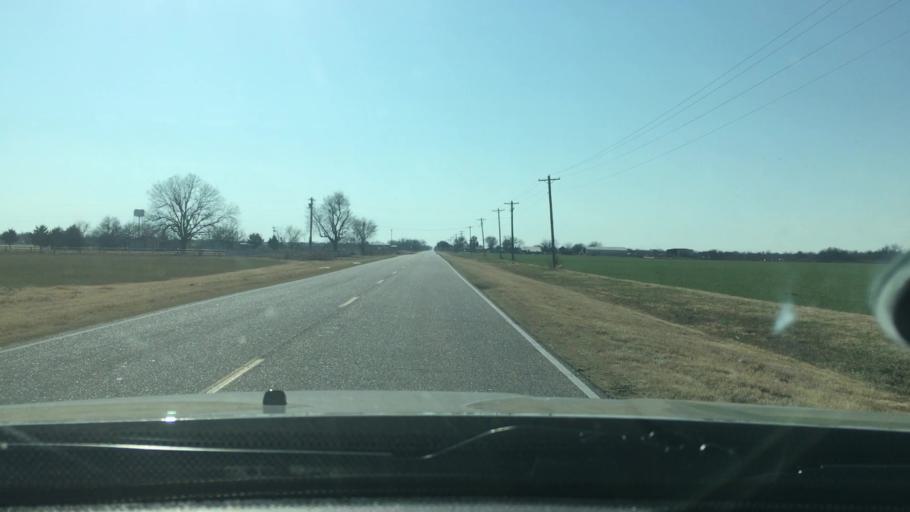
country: US
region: Oklahoma
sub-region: Garvin County
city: Stratford
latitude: 34.8178
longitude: -96.9677
